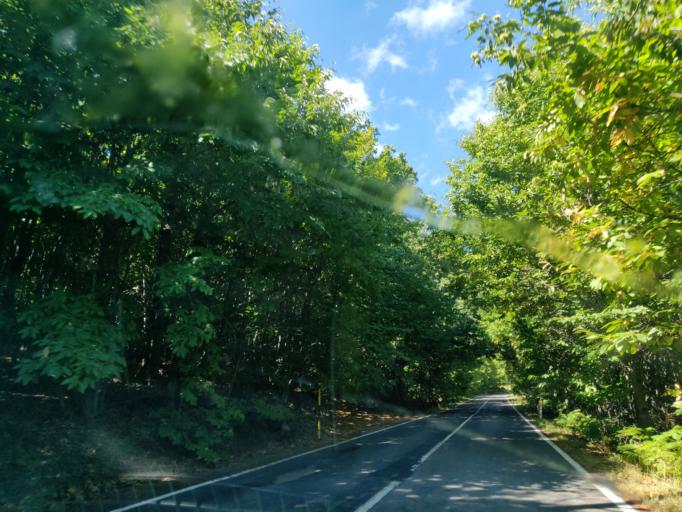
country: IT
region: Tuscany
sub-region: Provincia di Siena
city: Abbadia San Salvatore
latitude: 42.8946
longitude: 11.6540
